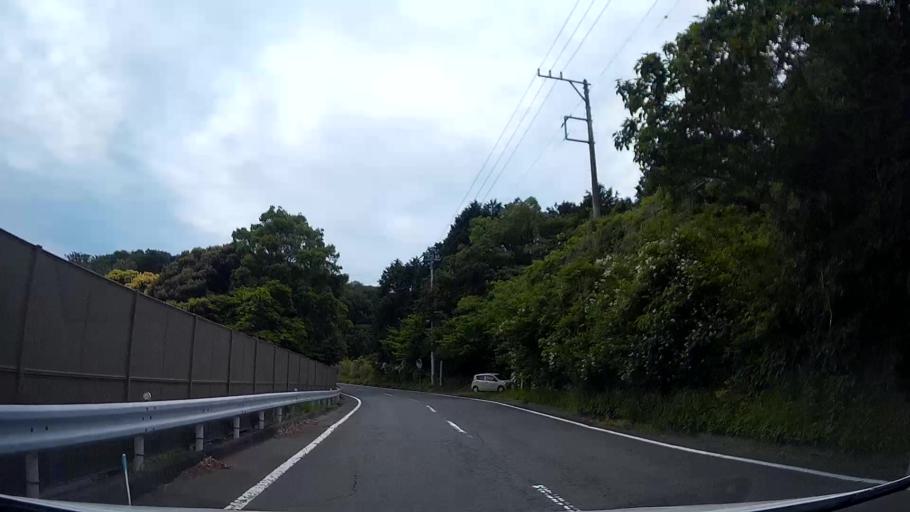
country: JP
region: Shizuoka
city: Ito
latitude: 34.9421
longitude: 139.1368
